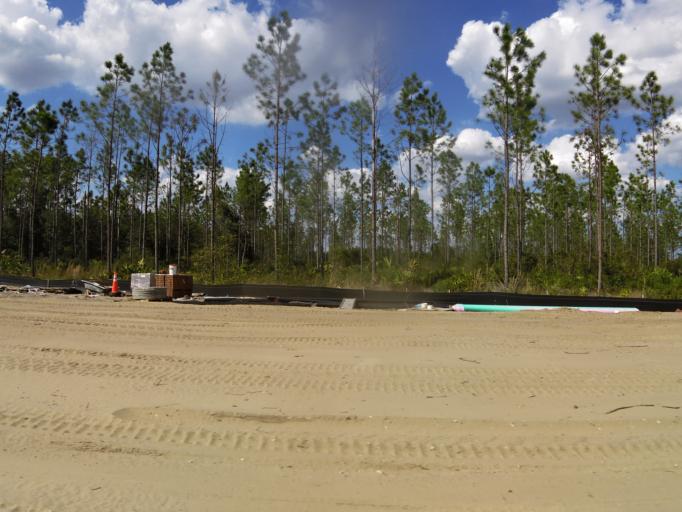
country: US
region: Florida
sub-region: Saint Johns County
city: Palm Valley
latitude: 30.1967
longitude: -81.5105
